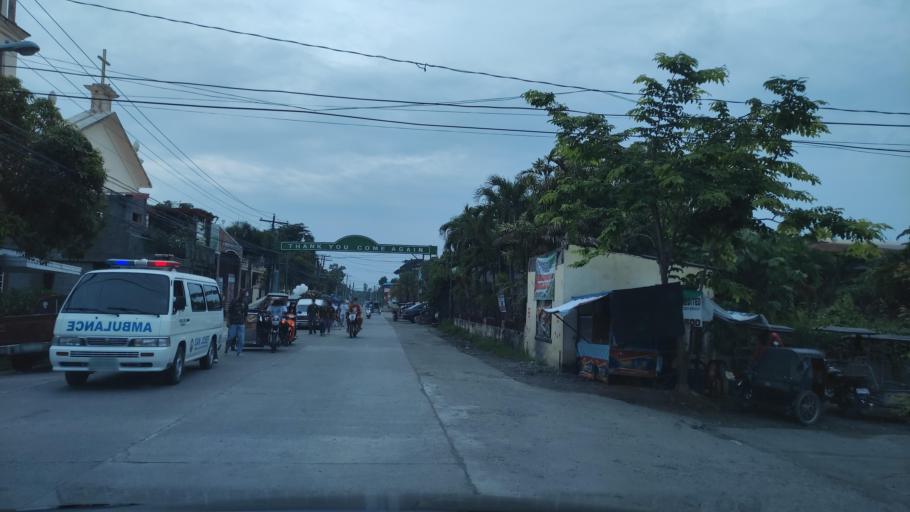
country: PH
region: Central Luzon
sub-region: Province of Nueva Ecija
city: San Anton
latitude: 15.3407
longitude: 120.9142
